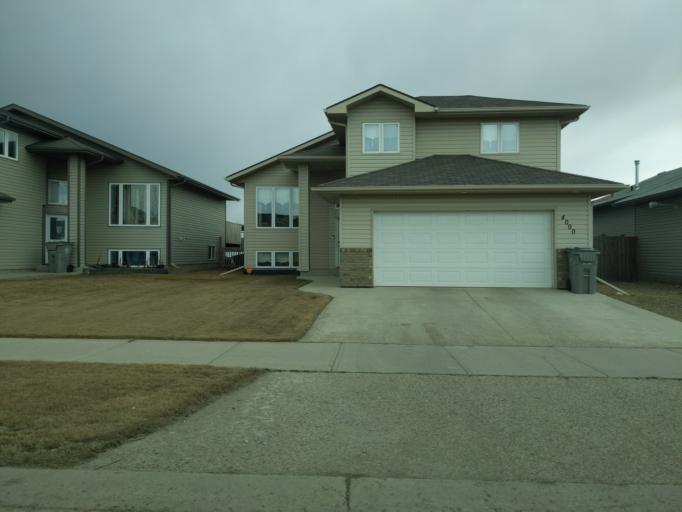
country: CA
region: Saskatchewan
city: Lloydminster
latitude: 53.2737
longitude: -110.0476
